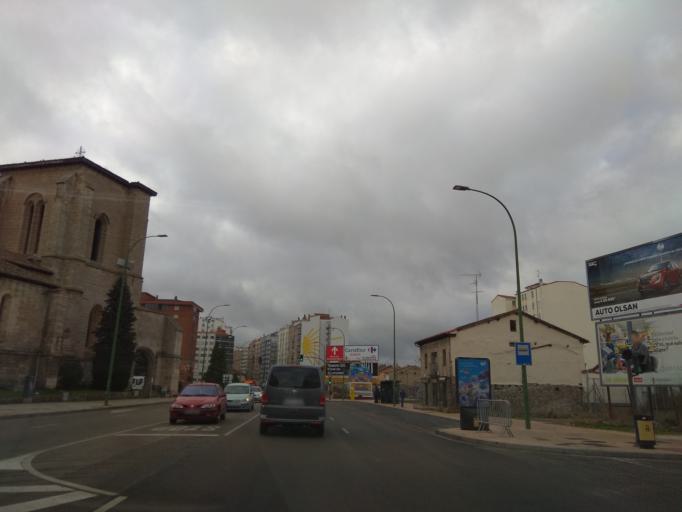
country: ES
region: Castille and Leon
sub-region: Provincia de Burgos
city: Burgos
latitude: 42.3543
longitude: -3.6663
